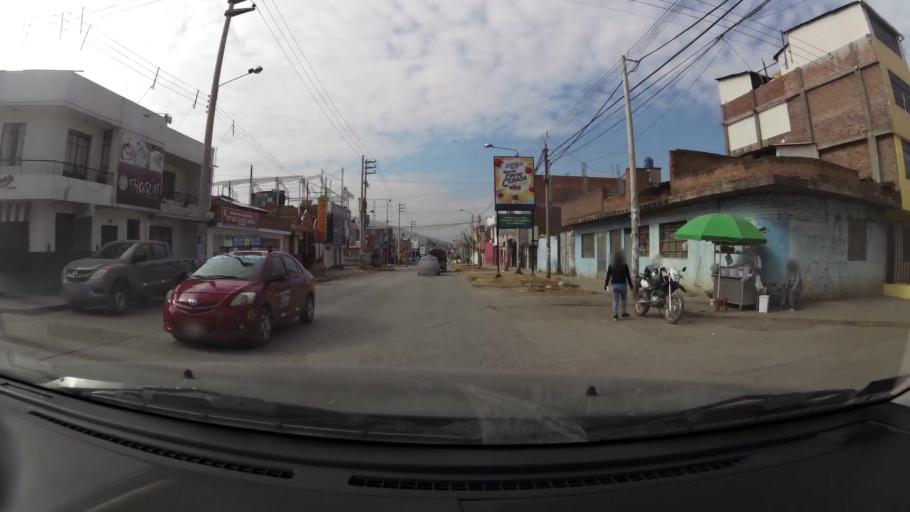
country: PE
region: Junin
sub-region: Provincia de Huancayo
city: Huancayo
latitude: -12.0580
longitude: -75.2037
